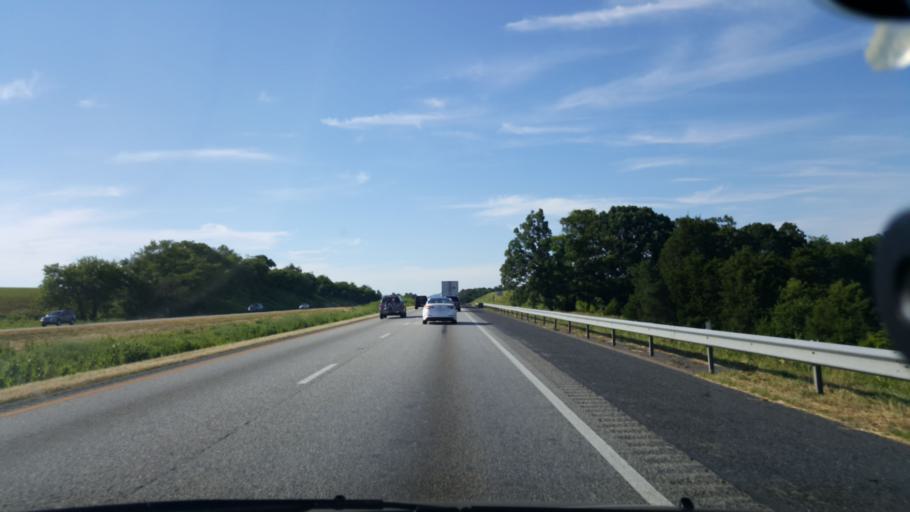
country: US
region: Virginia
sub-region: Augusta County
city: Weyers Cave
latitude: 38.3248
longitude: -78.9313
